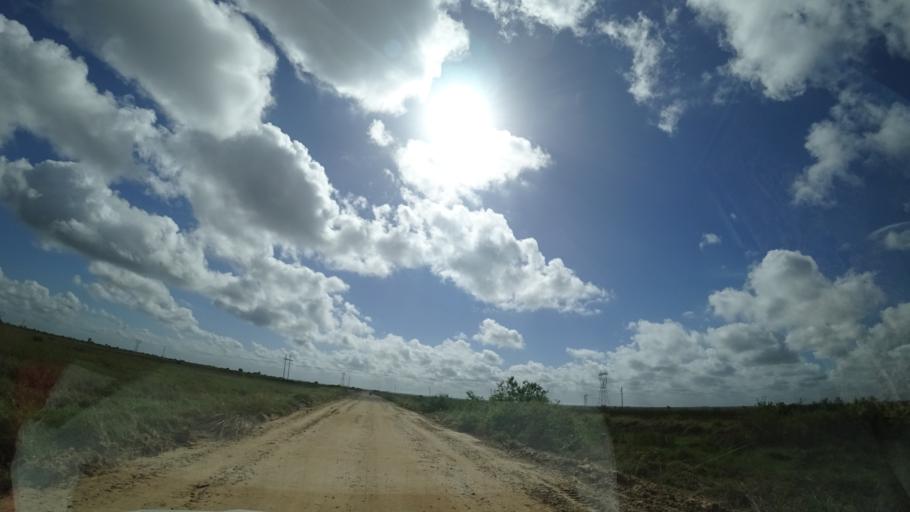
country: MZ
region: Sofala
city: Dondo
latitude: -19.4650
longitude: 34.5605
